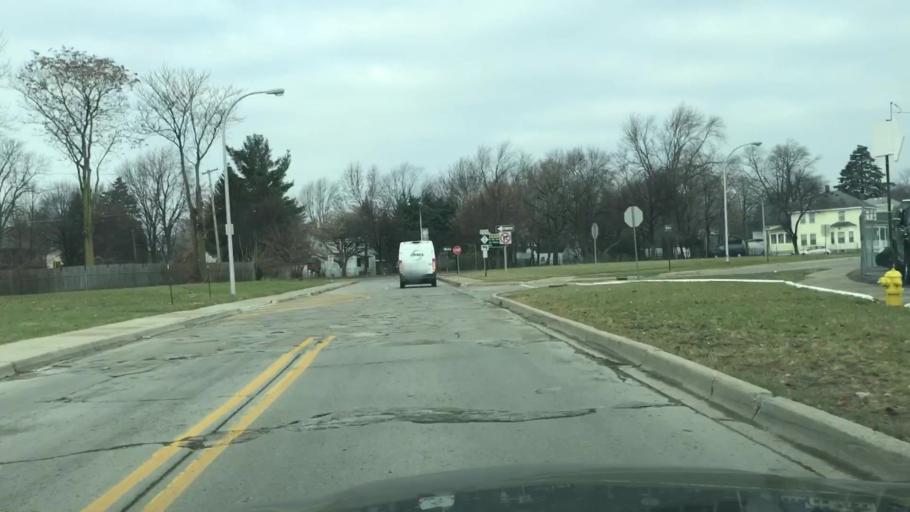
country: US
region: Michigan
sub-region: Macomb County
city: Mount Clemens
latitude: 42.6018
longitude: -82.8763
